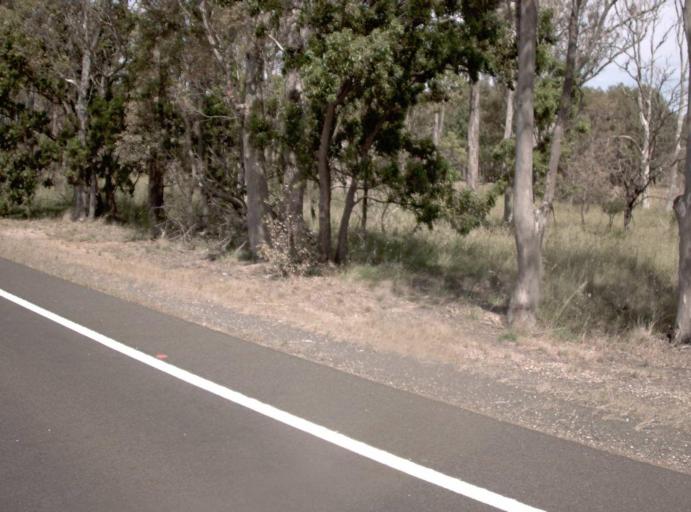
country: AU
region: Victoria
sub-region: East Gippsland
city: Bairnsdale
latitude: -37.8735
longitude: 147.4566
